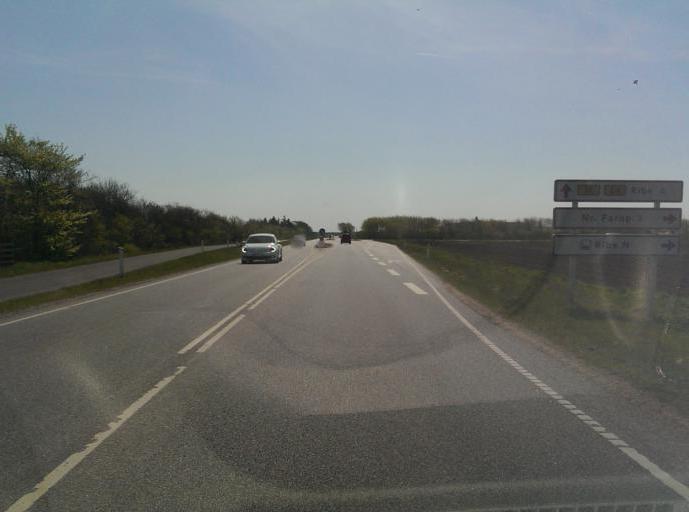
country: DK
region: South Denmark
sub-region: Esbjerg Kommune
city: Ribe
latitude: 55.3634
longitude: 8.7701
